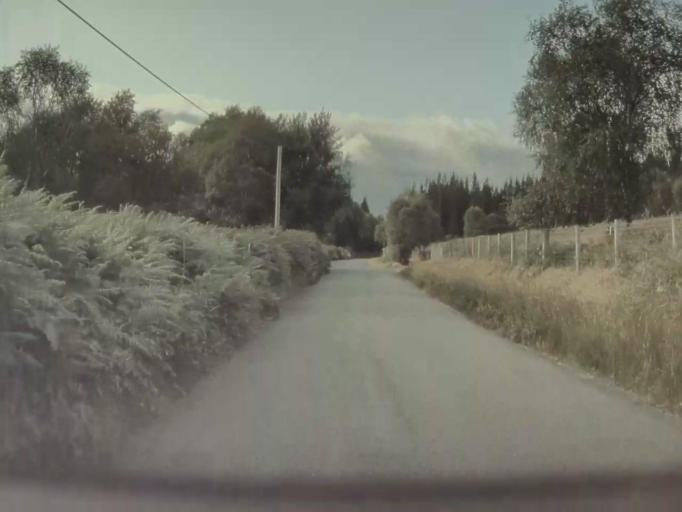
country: IE
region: Leinster
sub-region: Wicklow
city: Rathdrum
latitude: 53.0127
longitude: -6.2971
